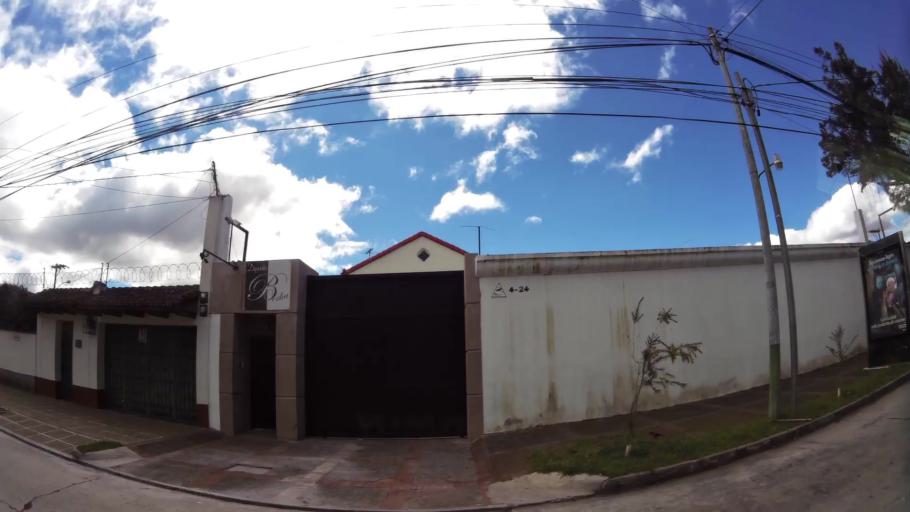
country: GT
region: Guatemala
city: Guatemala City
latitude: 14.6007
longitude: -90.5231
